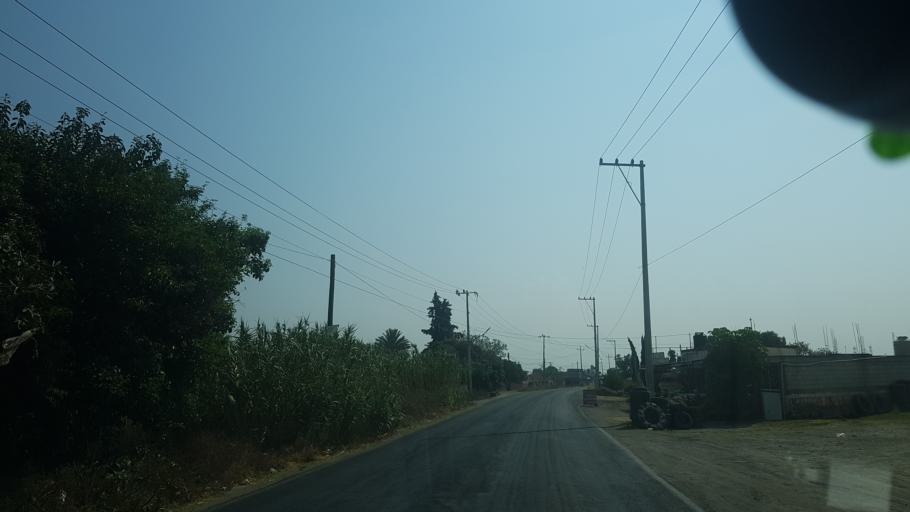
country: MX
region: Puebla
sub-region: San Jeronimo Tecuanipan
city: Los Reyes Tlanechicolpan
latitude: 19.0521
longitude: -98.3458
